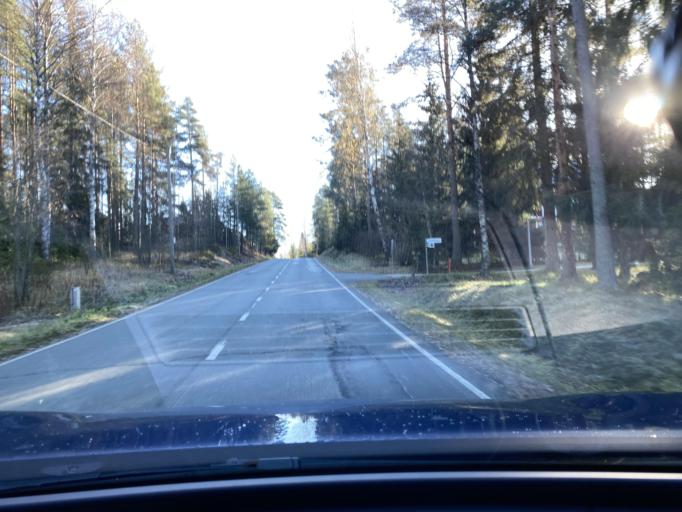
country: FI
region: Pirkanmaa
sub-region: Etelae-Pirkanmaa
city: Kylmaekoski
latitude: 61.0638
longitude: 23.6423
